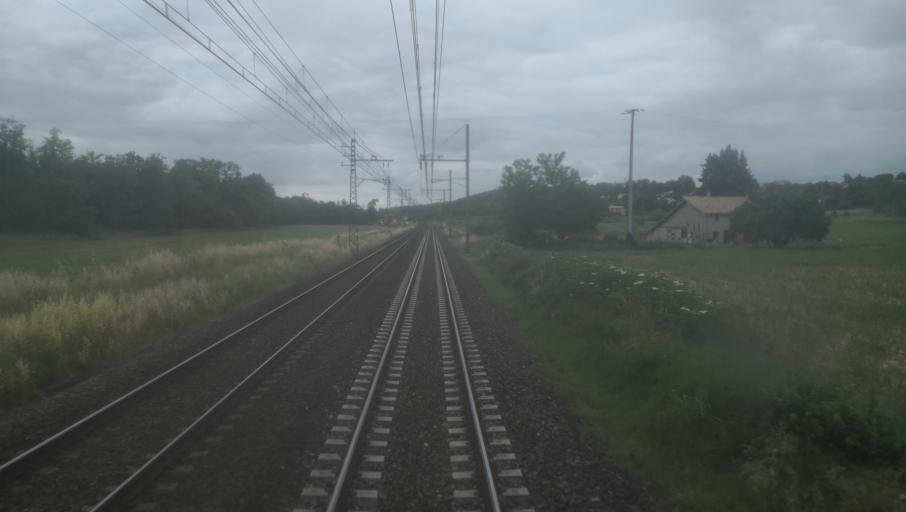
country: FR
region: Midi-Pyrenees
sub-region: Departement du Tarn-et-Garonne
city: Grisolles
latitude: 43.8474
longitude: 1.2890
